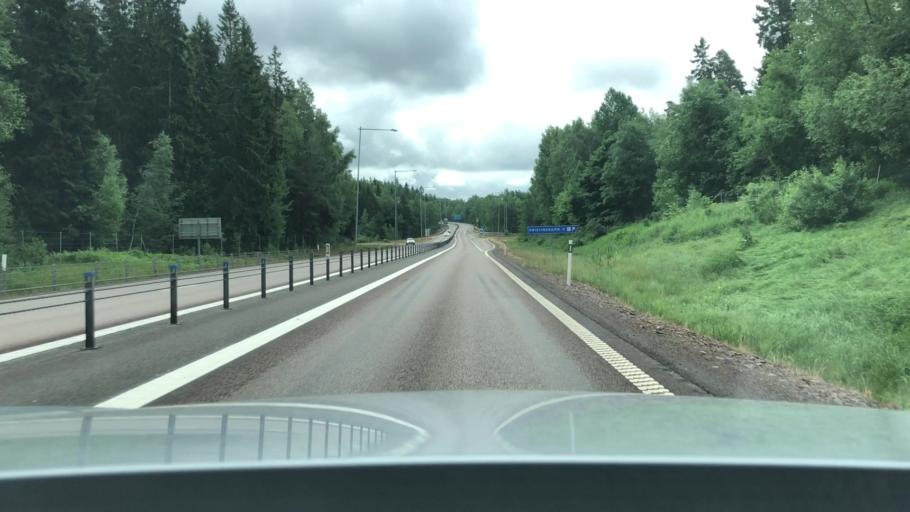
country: SE
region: Vaermland
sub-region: Kristinehamns Kommun
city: Kristinehamn
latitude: 59.3334
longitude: 14.0956
